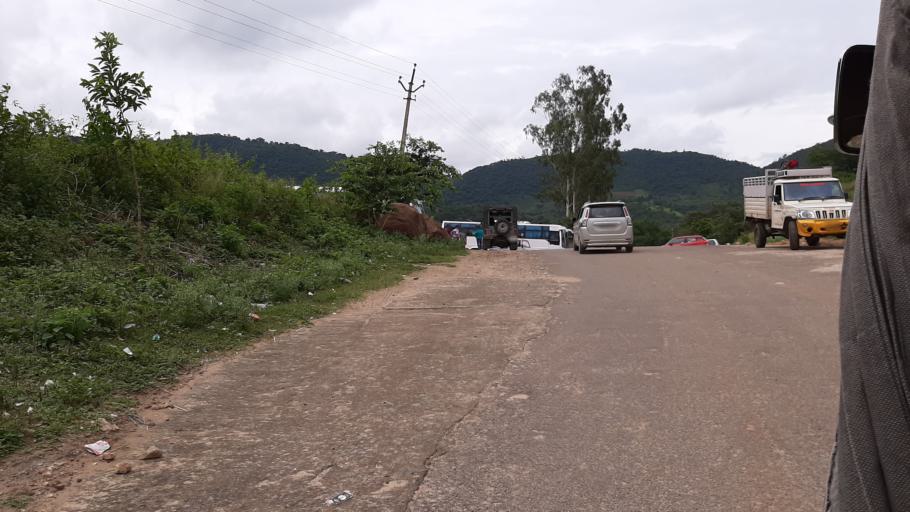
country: IN
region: Andhra Pradesh
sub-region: Vizianagaram District
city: Salur
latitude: 18.2779
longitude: 83.0377
